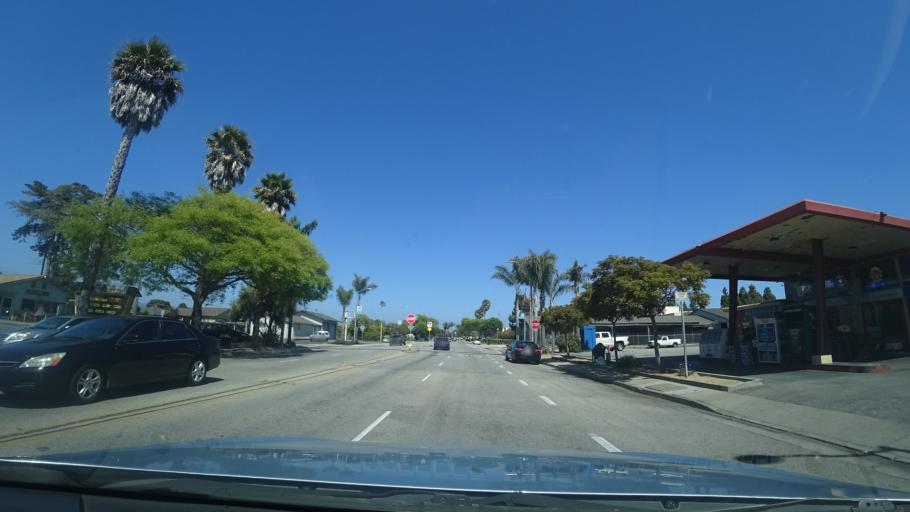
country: US
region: California
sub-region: Santa Cruz County
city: Opal Cliffs
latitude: 36.9634
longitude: -121.9680
